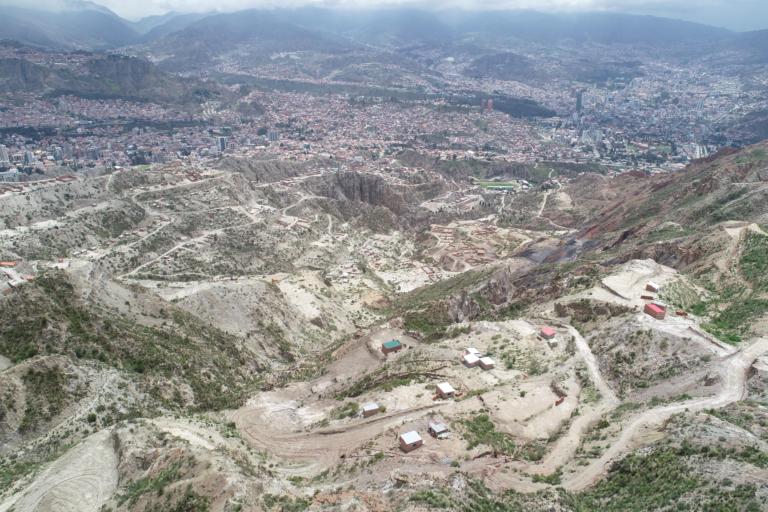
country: BO
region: La Paz
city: La Paz
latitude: -16.5451
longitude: -68.1180
